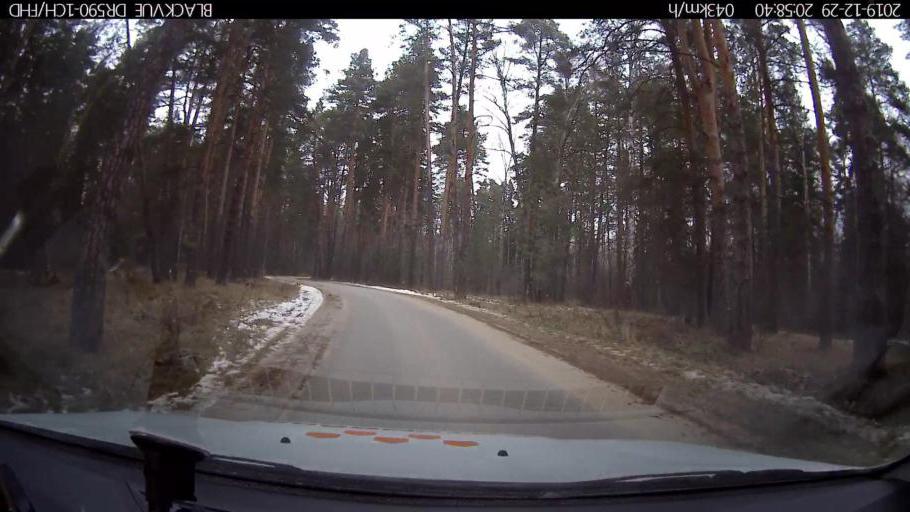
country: RU
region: Nizjnij Novgorod
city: Afonino
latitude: 56.1702
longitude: 43.9873
